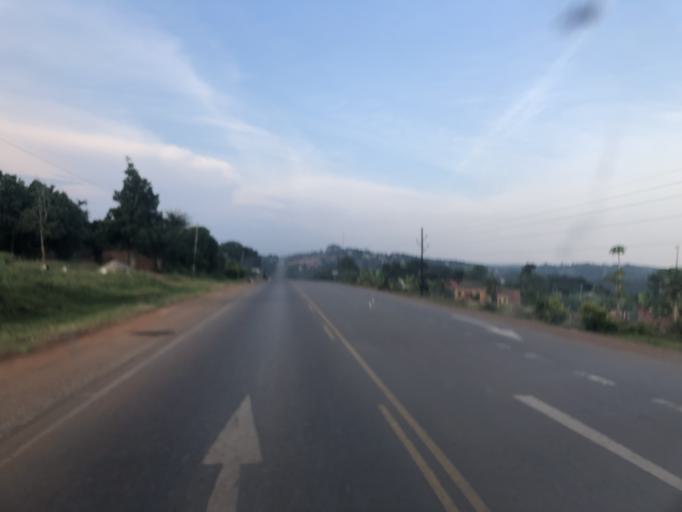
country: UG
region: Central Region
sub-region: Mpigi District
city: Mpigi
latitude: 0.2099
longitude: 32.3193
